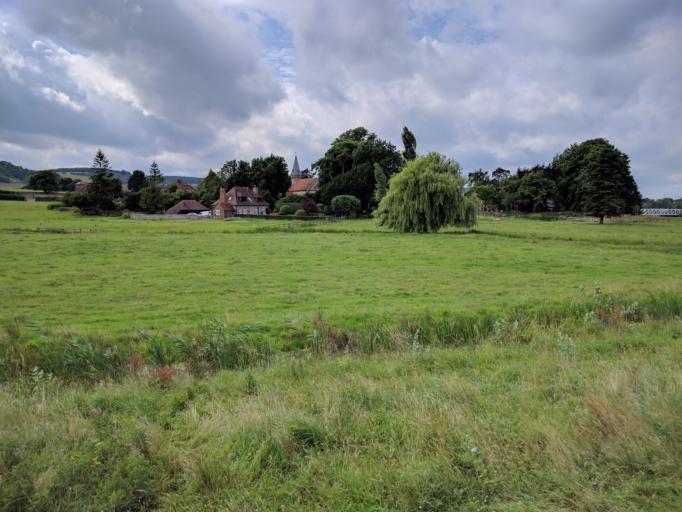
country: GB
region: England
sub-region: West Sussex
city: Arundel
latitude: 50.8801
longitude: -0.5396
